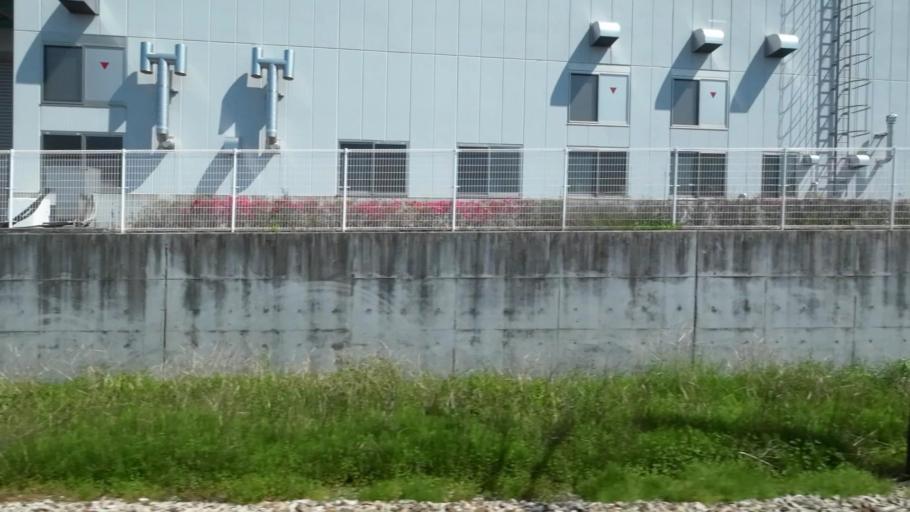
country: JP
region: Hiroshima
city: Fukuyama
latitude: 34.4781
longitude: 133.3159
